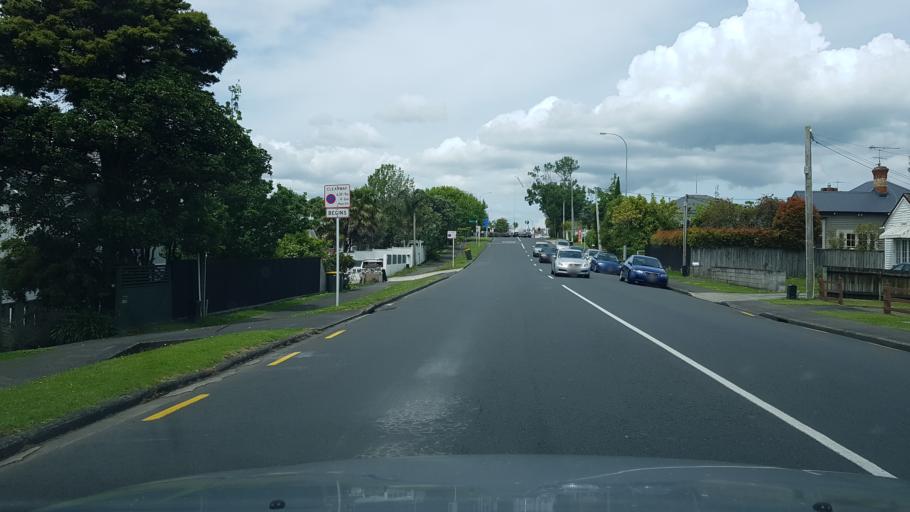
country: NZ
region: Auckland
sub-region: Auckland
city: North Shore
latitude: -36.8077
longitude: 174.7256
